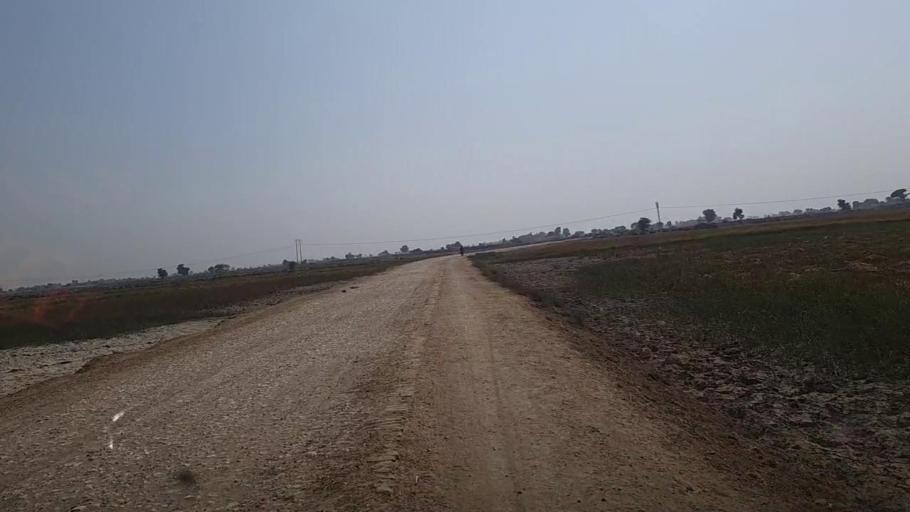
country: PK
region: Sindh
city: Kandhkot
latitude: 28.3914
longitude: 69.2934
